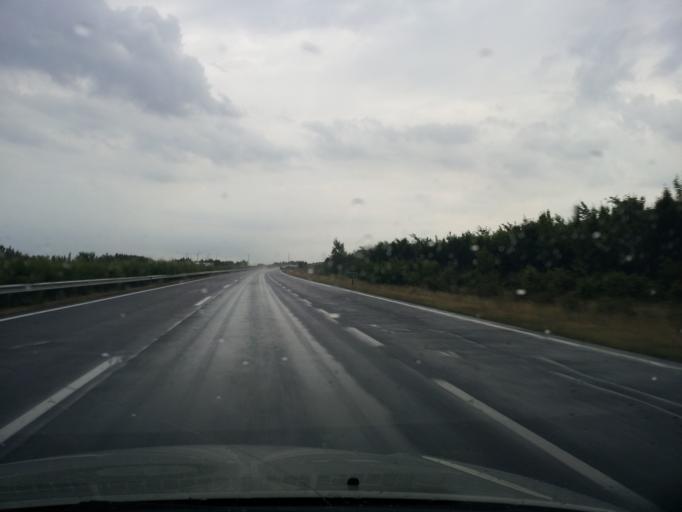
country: HU
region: Borsod-Abauj-Zemplen
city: Onod
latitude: 47.9665
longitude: 20.8956
